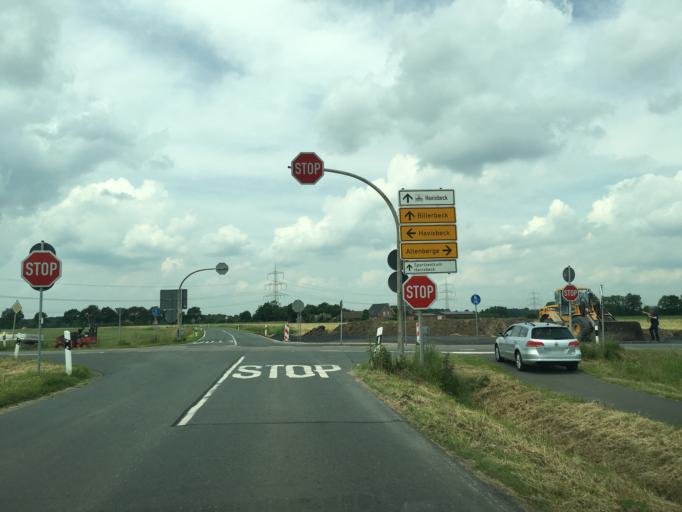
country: DE
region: North Rhine-Westphalia
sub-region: Regierungsbezirk Munster
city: Havixbeck
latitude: 51.9960
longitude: 7.4395
